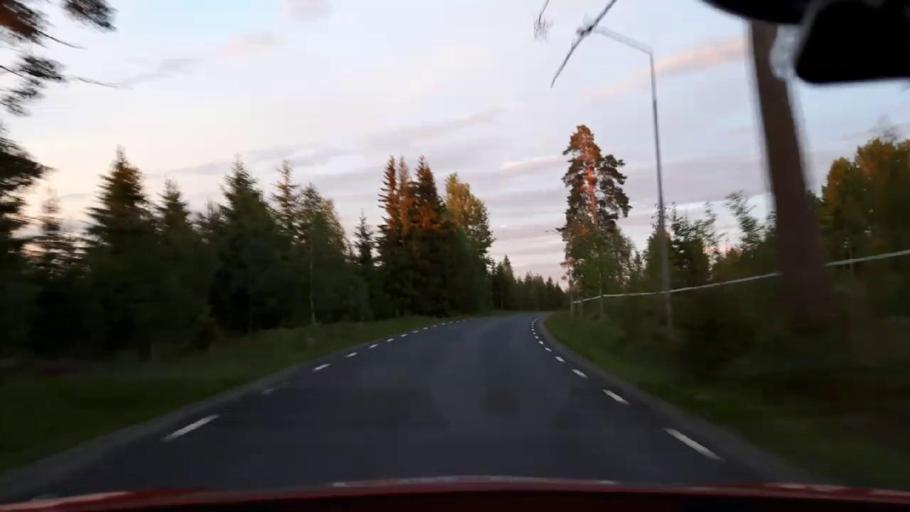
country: SE
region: Jaemtland
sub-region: OEstersunds Kommun
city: Brunflo
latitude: 63.0536
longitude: 14.8224
